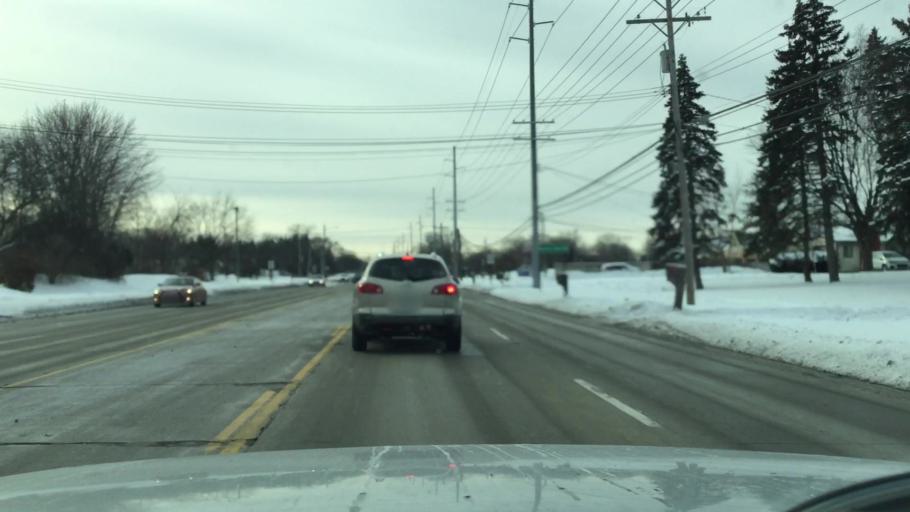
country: US
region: Michigan
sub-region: Oakland County
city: Troy
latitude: 42.6092
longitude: -83.1300
